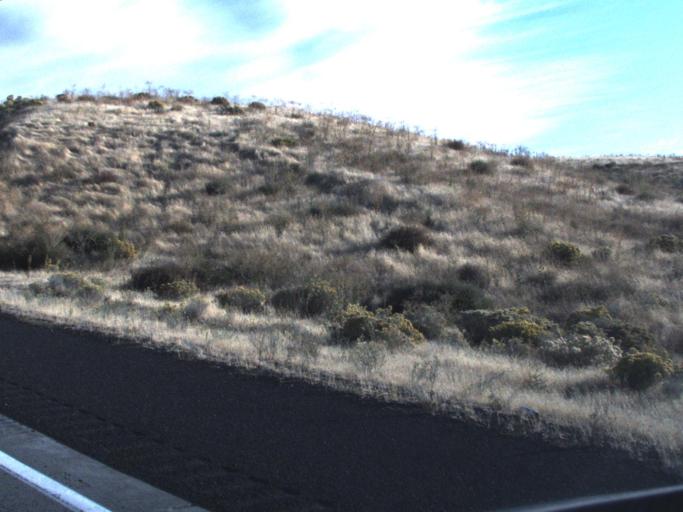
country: US
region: Washington
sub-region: Franklin County
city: Connell
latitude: 46.6896
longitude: -118.8388
